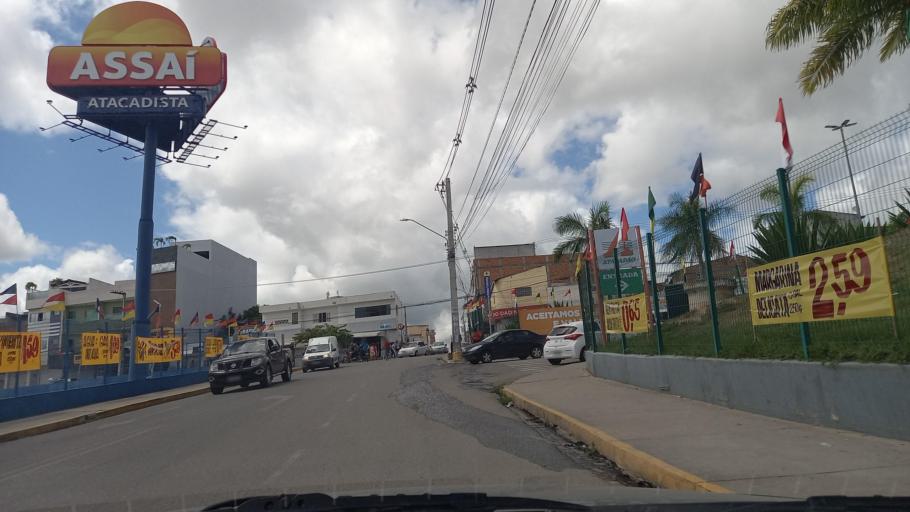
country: BR
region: Pernambuco
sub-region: Caruaru
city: Caruaru
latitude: -8.2960
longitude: -35.9710
